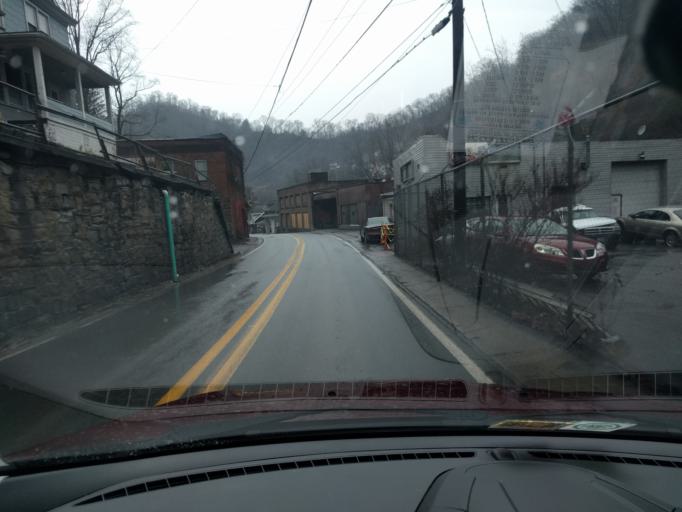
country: US
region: West Virginia
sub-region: McDowell County
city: Welch
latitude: 37.4340
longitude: -81.5751
